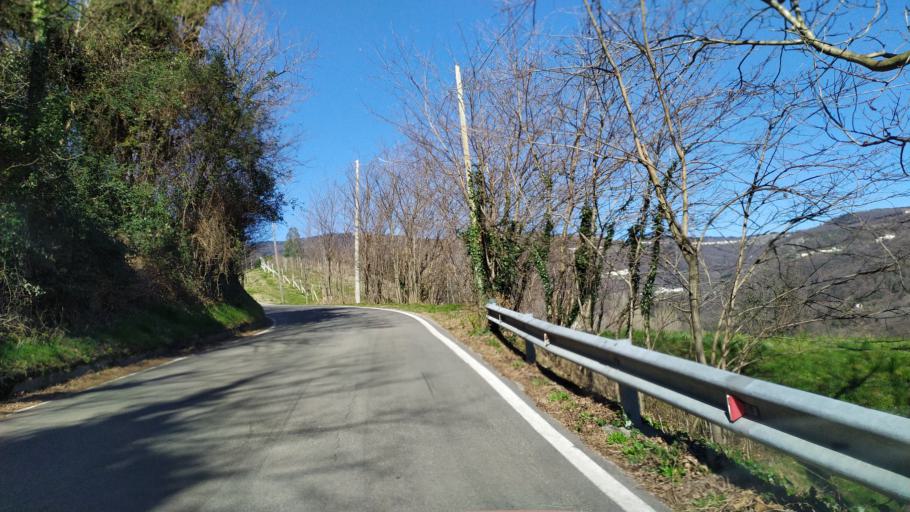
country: IT
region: Veneto
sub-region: Provincia di Vicenza
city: Fara Vicentino
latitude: 45.7518
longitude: 11.5428
